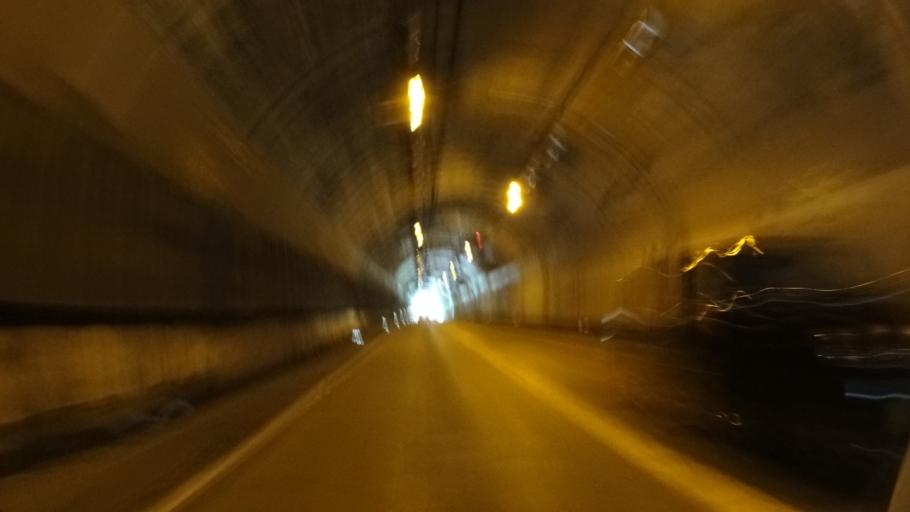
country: JP
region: Oita
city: Tsukawaki
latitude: 33.2532
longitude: 131.3002
